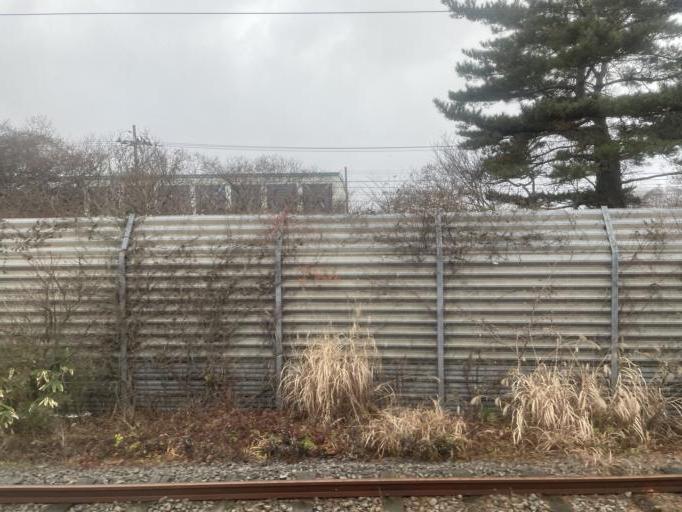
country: JP
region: Aomori
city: Aomori Shi
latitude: 40.9868
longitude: 140.6526
